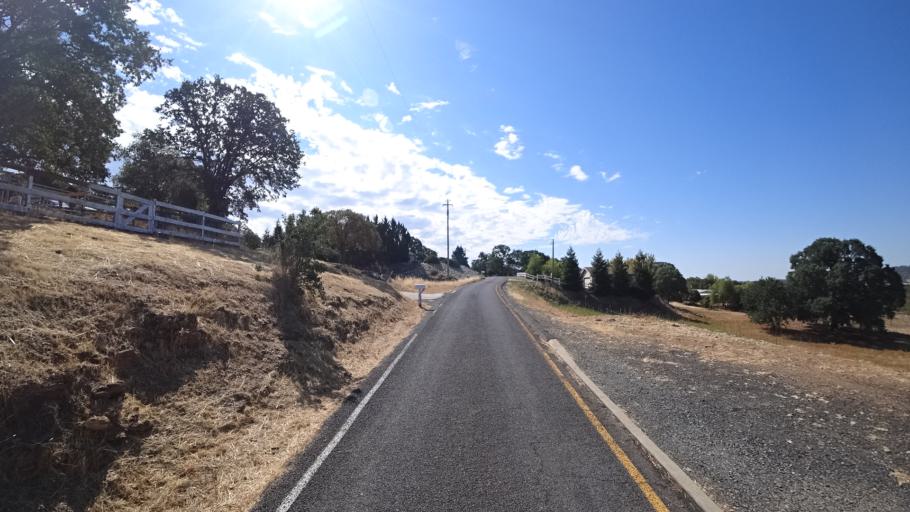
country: US
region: California
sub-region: Calaveras County
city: Copperopolis
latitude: 37.9215
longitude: -120.6285
